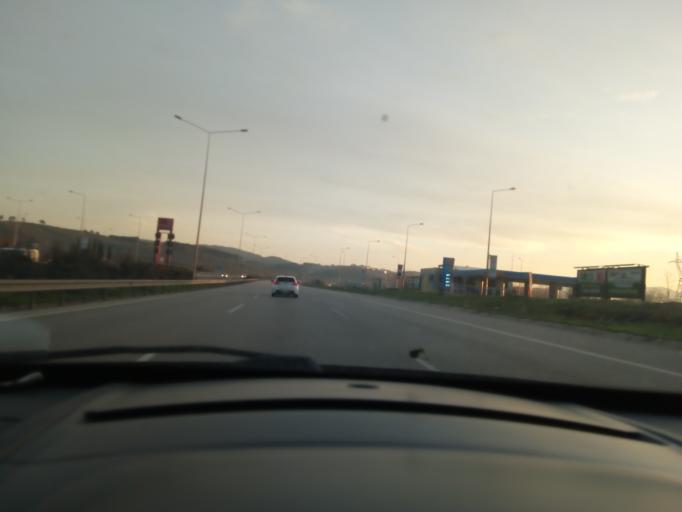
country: TR
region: Bursa
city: Niluefer
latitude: 40.2821
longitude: 28.9955
